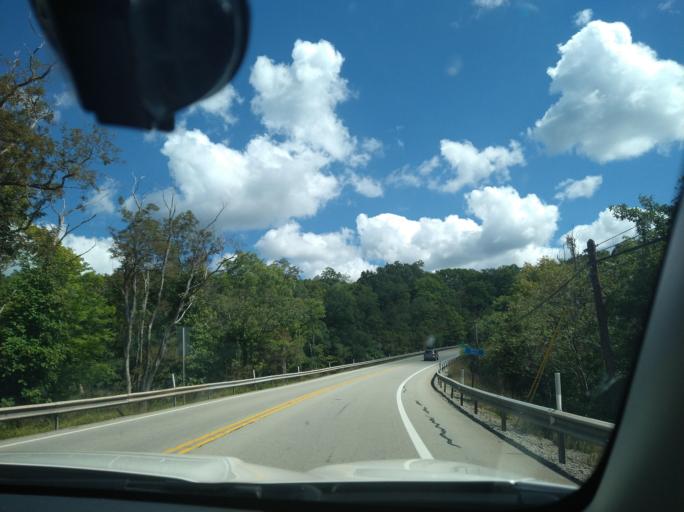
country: US
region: Pennsylvania
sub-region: Fayette County
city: Bear Rocks
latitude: 40.0880
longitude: -79.3354
